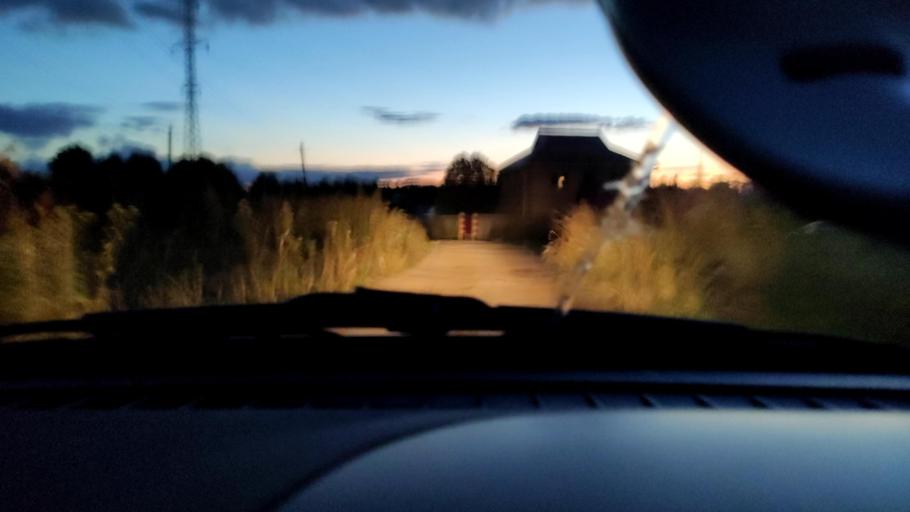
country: RU
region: Perm
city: Froly
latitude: 57.9467
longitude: 56.2489
